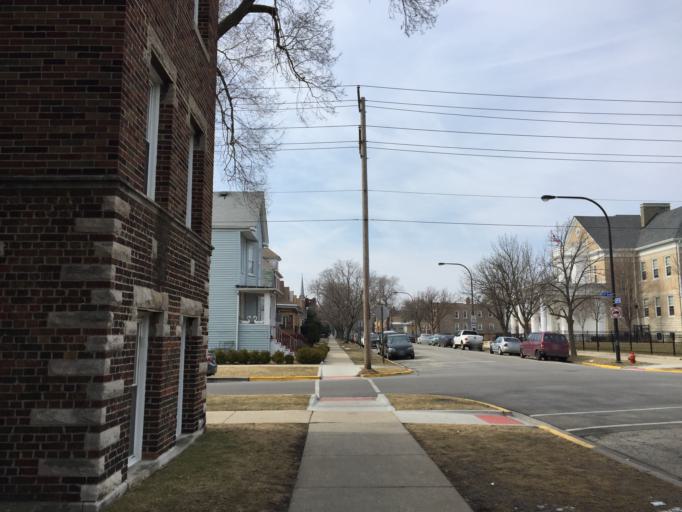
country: US
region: Illinois
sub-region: Cook County
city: Cicero
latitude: 41.8474
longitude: -87.7513
